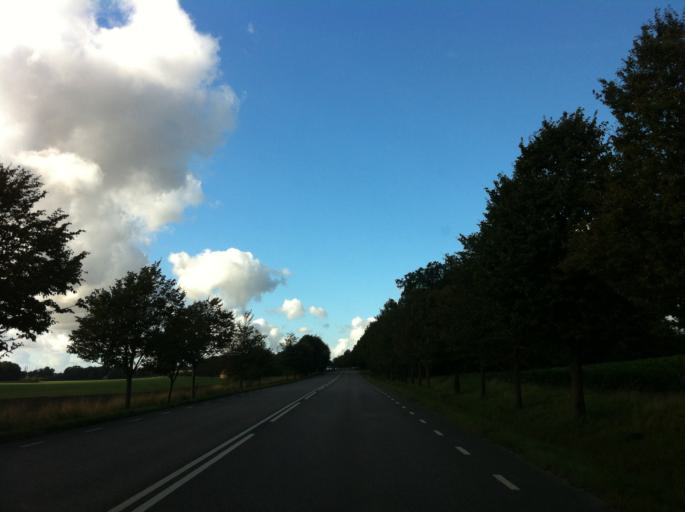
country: SE
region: Skane
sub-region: Eslovs Kommun
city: Eslov
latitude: 55.7725
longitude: 13.3133
